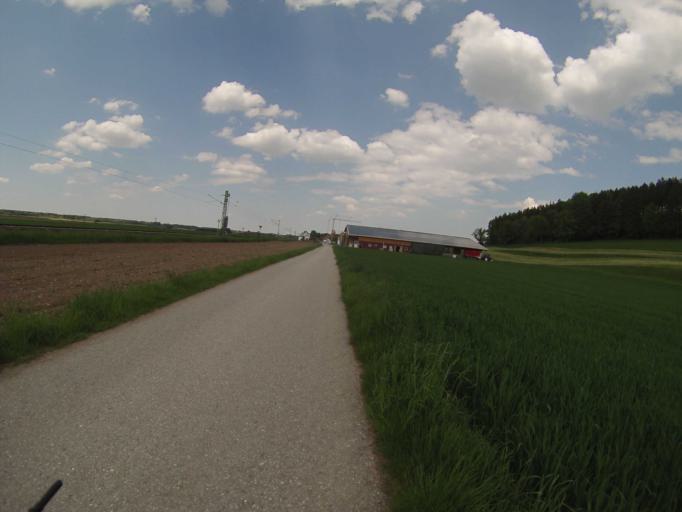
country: DE
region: Bavaria
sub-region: Upper Bavaria
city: Aying
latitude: 47.9570
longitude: 11.7789
